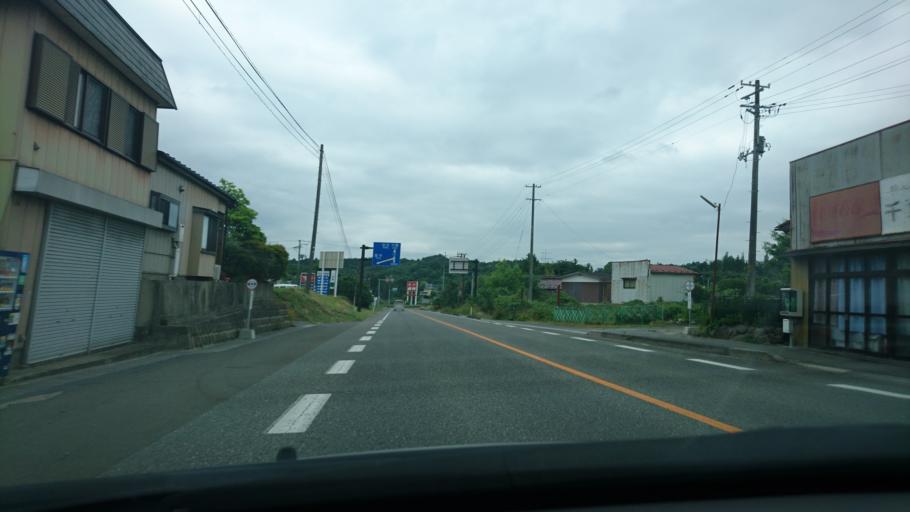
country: JP
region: Miyagi
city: Furukawa
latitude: 38.7238
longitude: 141.0221
